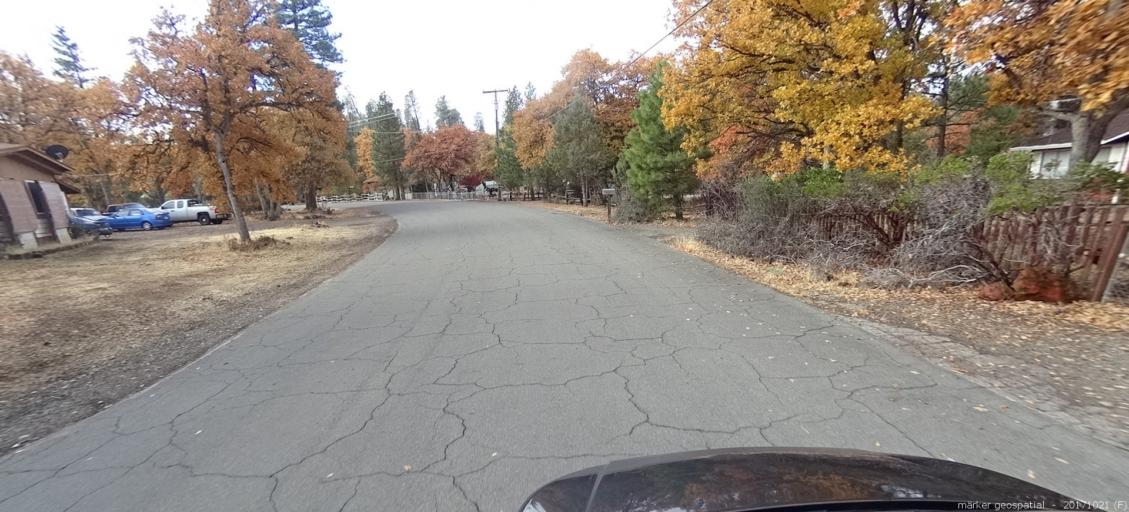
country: US
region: California
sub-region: Shasta County
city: Burney
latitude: 40.9185
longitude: -121.5598
